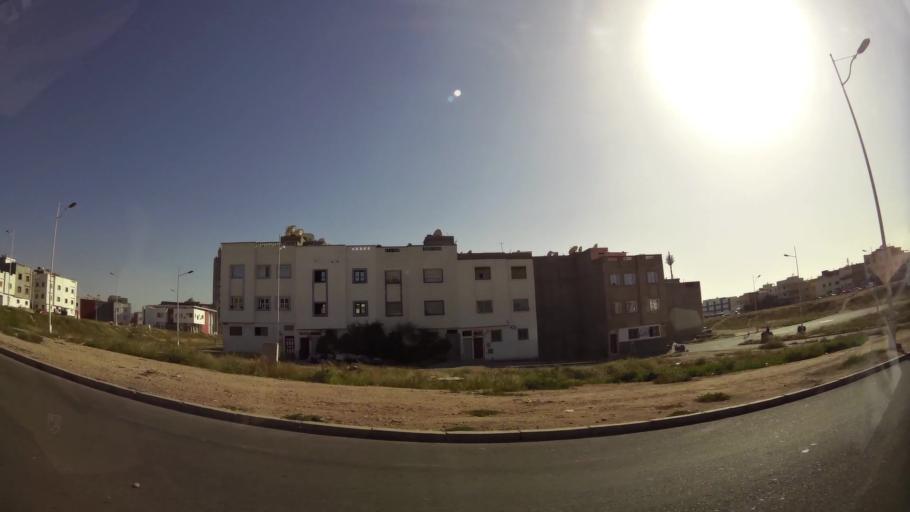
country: MA
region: Souss-Massa-Draa
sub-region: Agadir-Ida-ou-Tnan
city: Agadir
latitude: 30.4255
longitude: -9.5749
